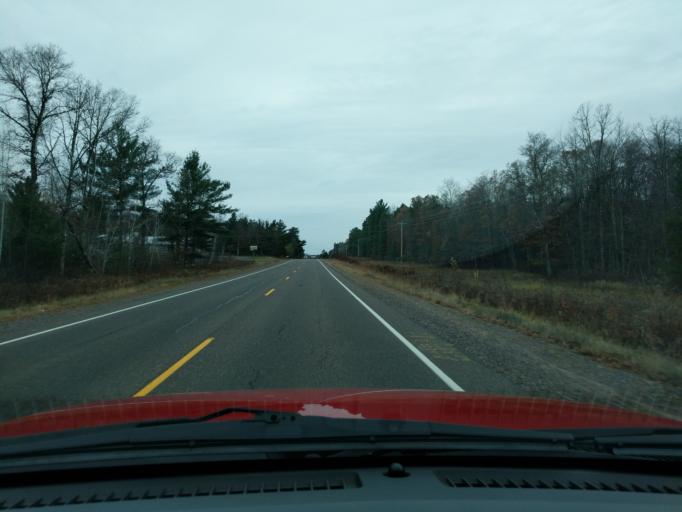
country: US
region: Wisconsin
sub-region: Burnett County
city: Siren
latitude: 45.8248
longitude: -92.3085
